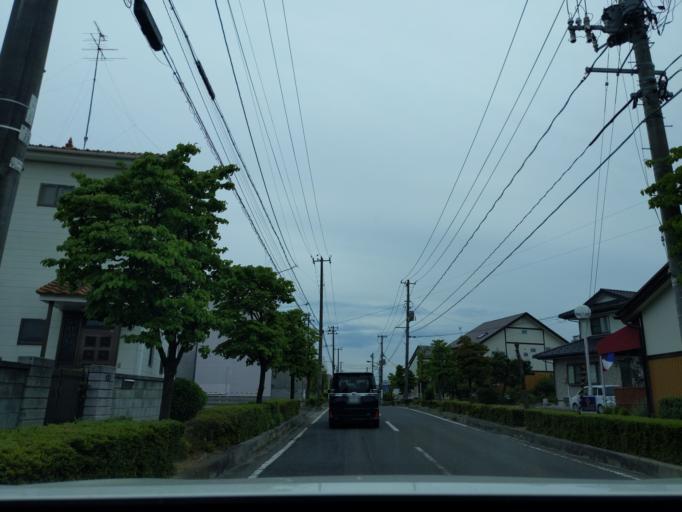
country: JP
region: Fukushima
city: Koriyama
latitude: 37.3761
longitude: 140.3662
